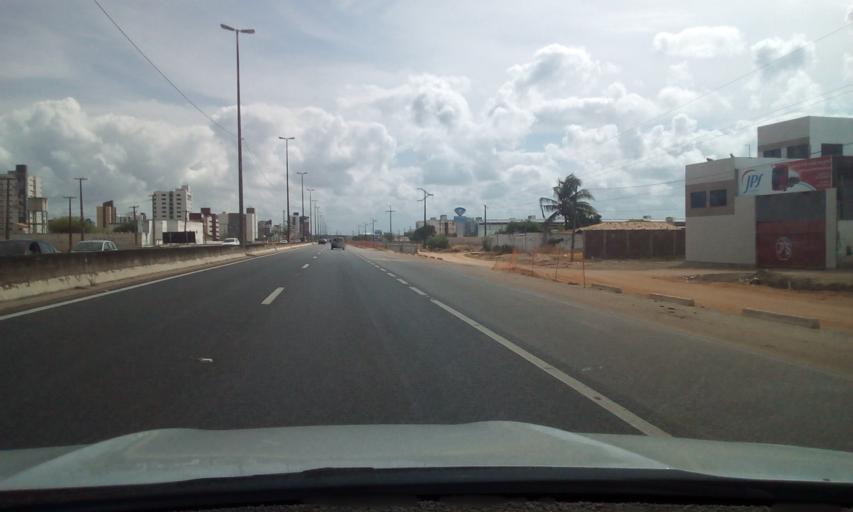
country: BR
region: Paraiba
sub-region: Cabedelo
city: Cabedelo
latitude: -7.0325
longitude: -34.8416
